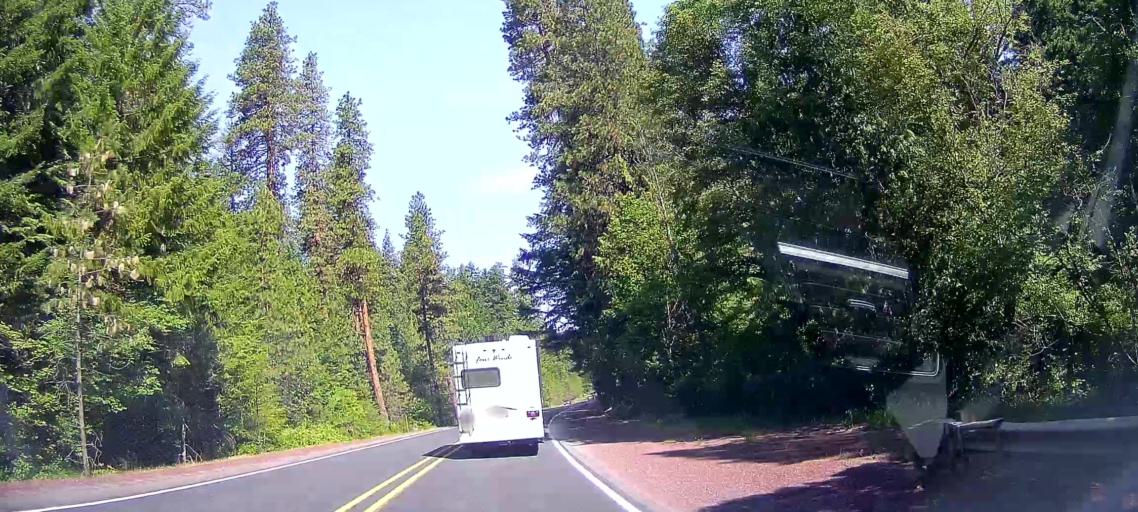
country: US
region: Oregon
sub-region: Jefferson County
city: Warm Springs
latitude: 45.0743
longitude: -121.5354
